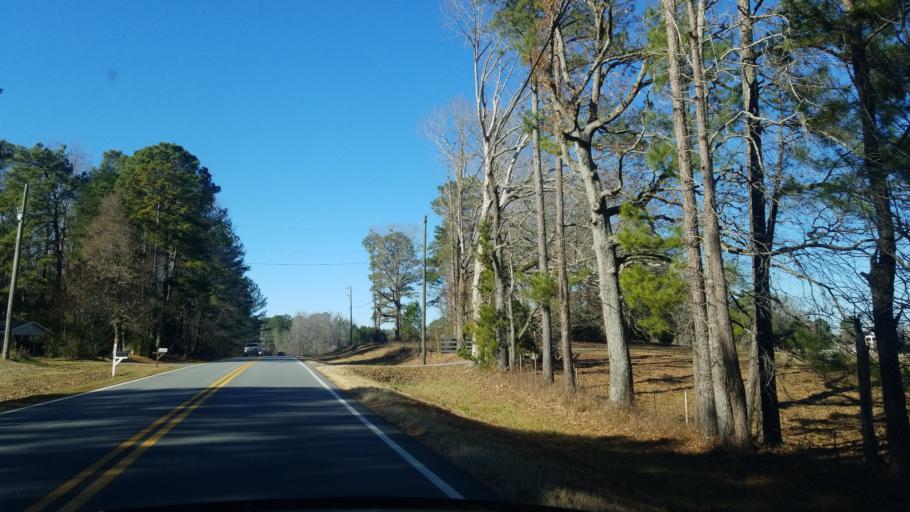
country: US
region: Georgia
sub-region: Harris County
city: Hamilton
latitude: 32.6716
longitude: -84.9051
